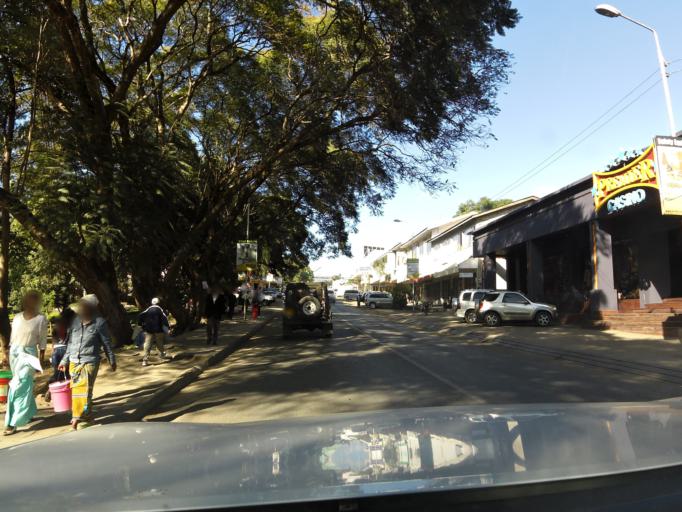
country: TZ
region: Arusha
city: Arusha
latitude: -3.3735
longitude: 36.6909
